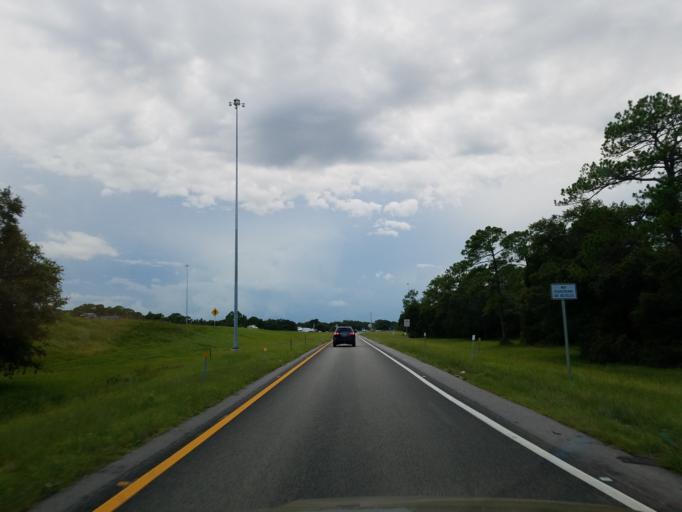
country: US
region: Florida
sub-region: Sarasota County
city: North Port
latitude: 27.1000
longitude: -82.2045
